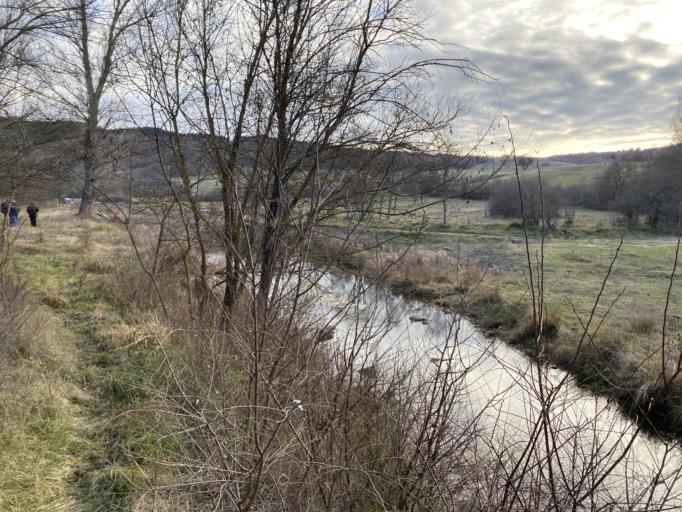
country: MK
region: Opstina Rankovce
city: Rankovce
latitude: 42.1550
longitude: 22.0813
